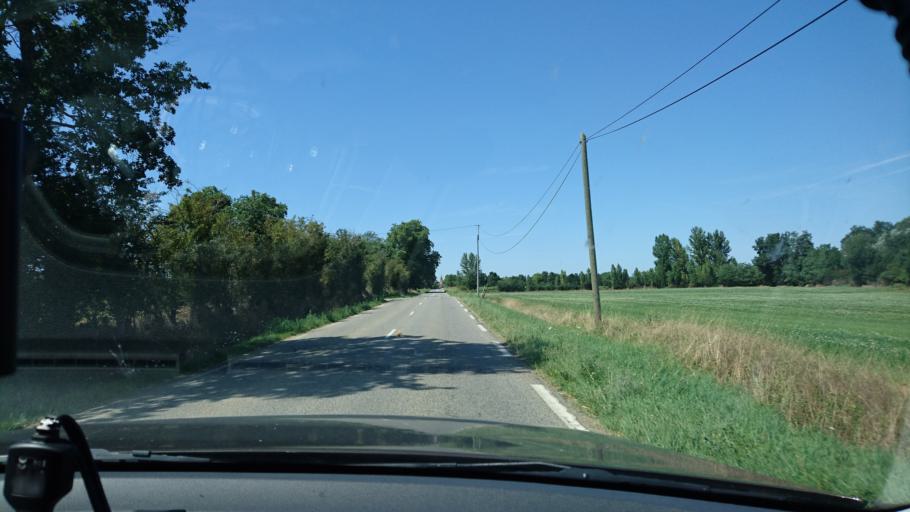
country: FR
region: Midi-Pyrenees
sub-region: Departement de l'Ariege
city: Lezat-sur-Leze
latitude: 43.2623
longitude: 1.3555
